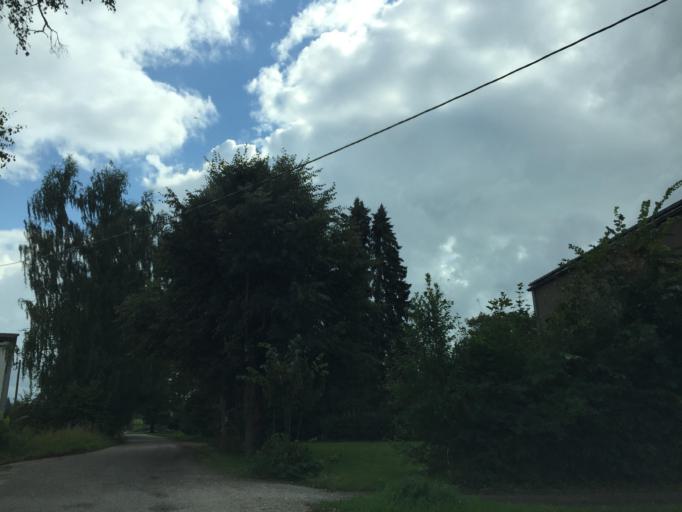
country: LV
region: Raunas
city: Rauna
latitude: 57.3363
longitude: 25.4871
